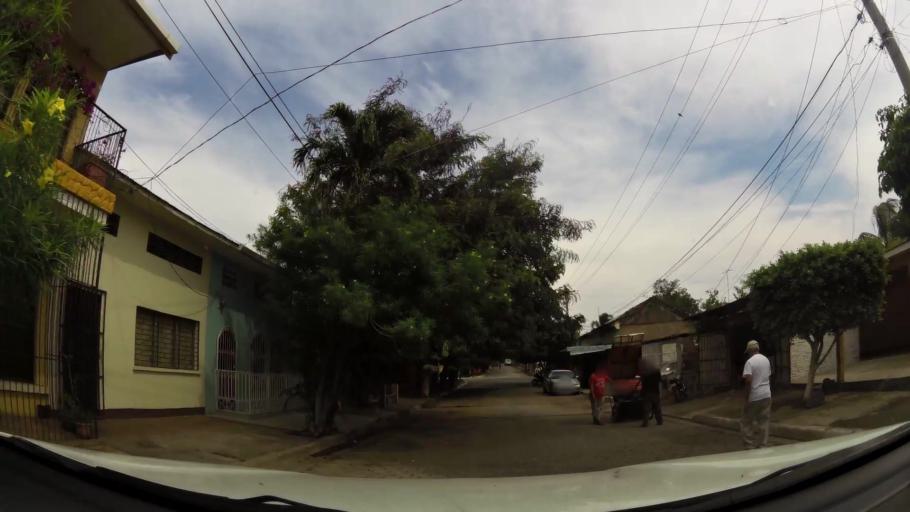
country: NI
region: Rivas
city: Rivas
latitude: 11.4355
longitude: -85.8304
